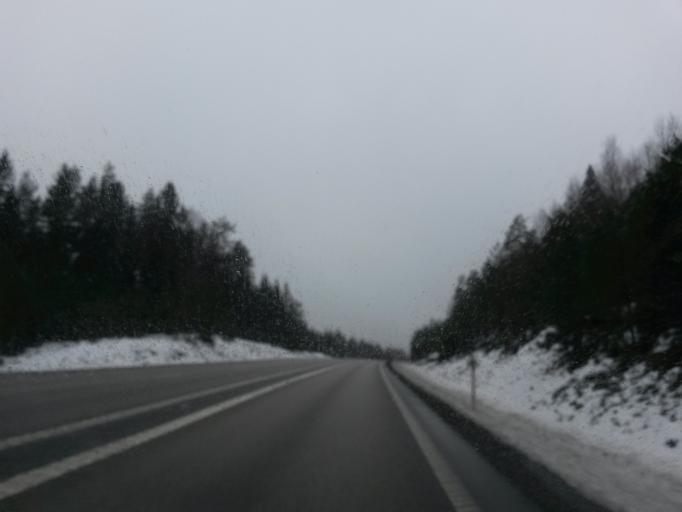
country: SE
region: Vaestra Goetaland
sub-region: Marks Kommun
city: Fritsla
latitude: 57.5433
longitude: 12.8141
